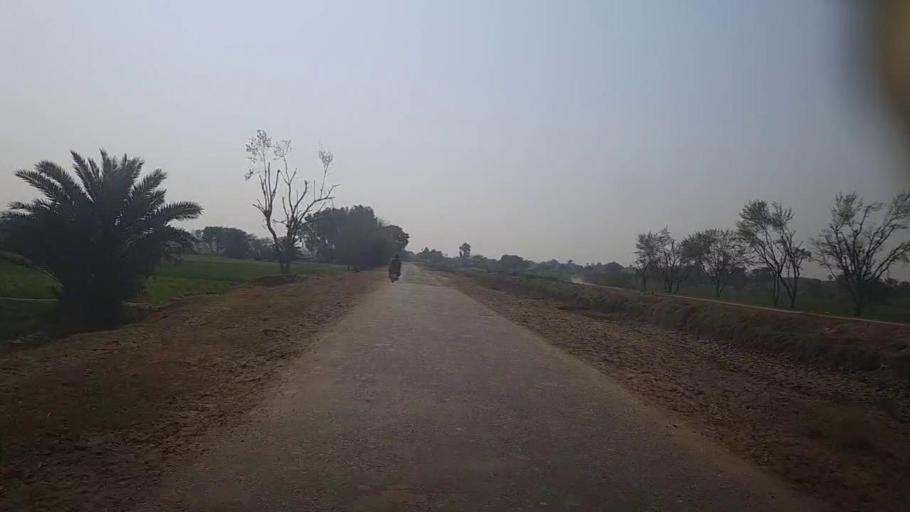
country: PK
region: Sindh
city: Kot Diji
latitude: 27.3686
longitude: 68.7493
